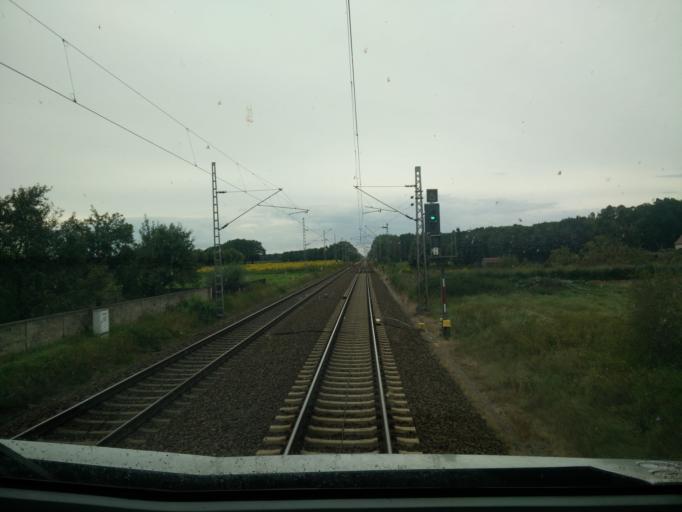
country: DE
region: Brandenburg
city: Paulinenaue
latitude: 52.6785
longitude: 12.7090
